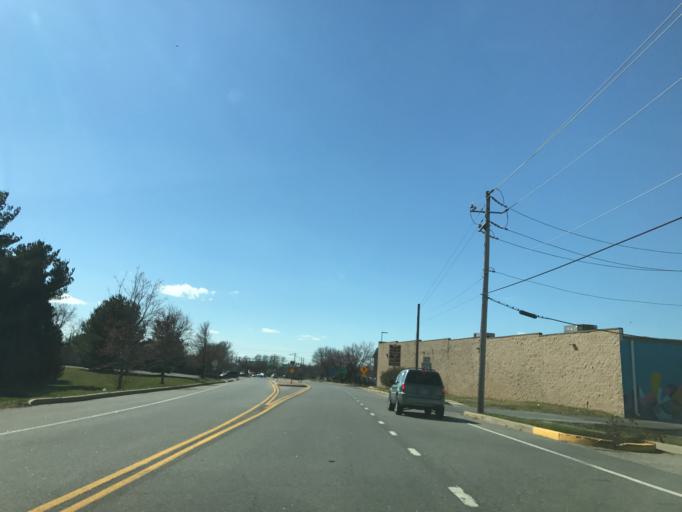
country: US
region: Maryland
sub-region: Kent County
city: Chestertown
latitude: 39.2240
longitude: -76.0670
